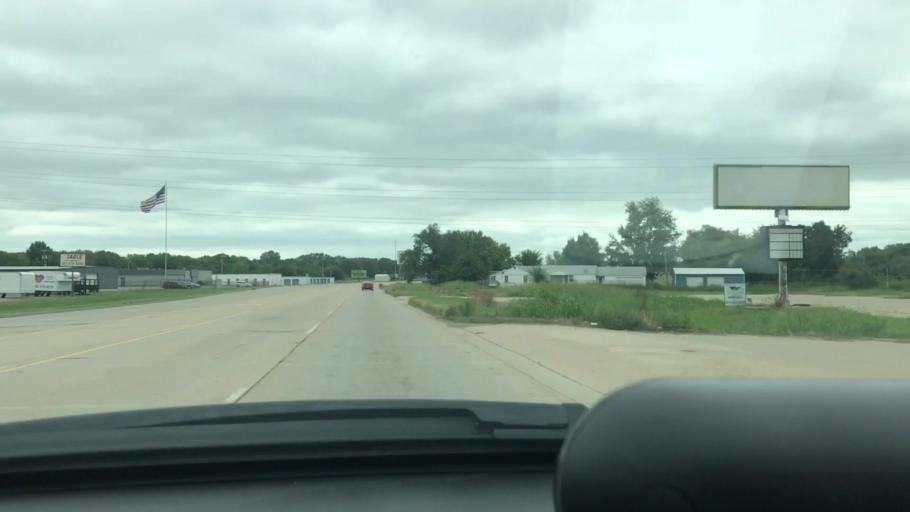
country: US
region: Oklahoma
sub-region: Mayes County
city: Chouteau
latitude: 36.1776
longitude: -95.3425
